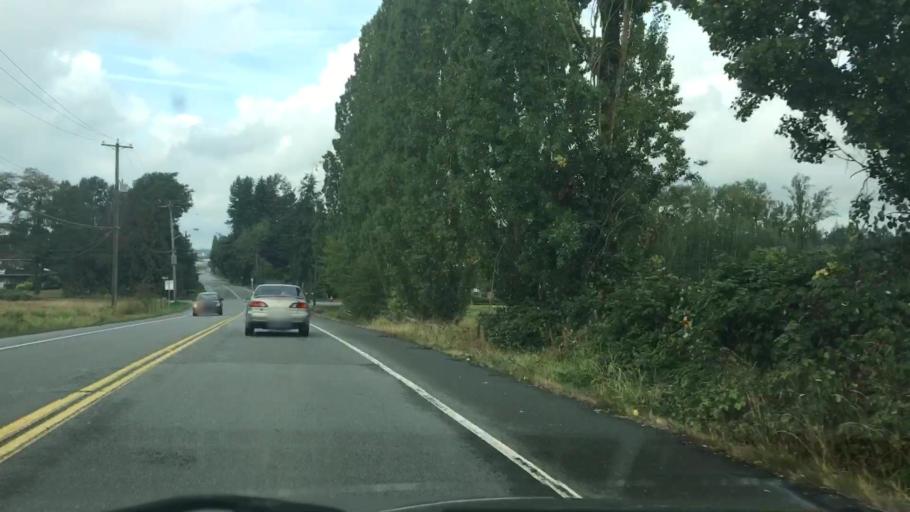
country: CA
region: British Columbia
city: Langley
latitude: 49.1045
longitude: -122.6027
